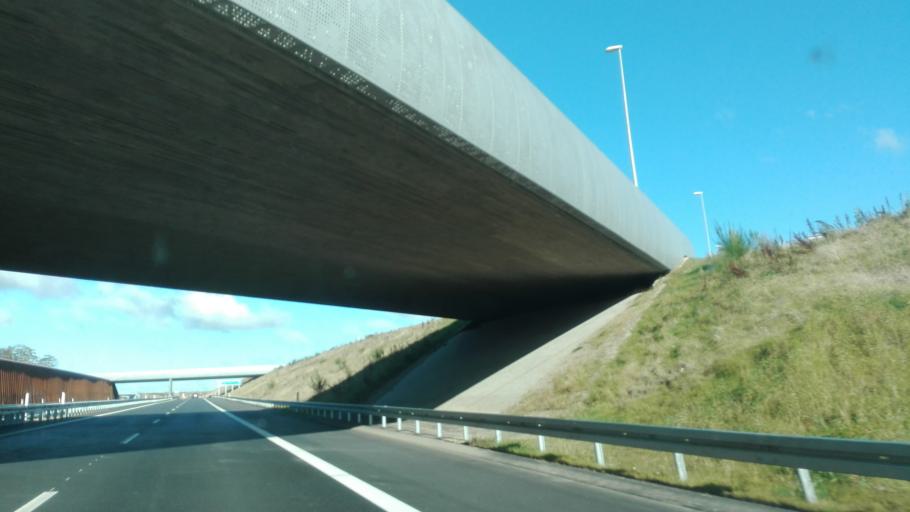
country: DK
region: Central Jutland
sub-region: Silkeborg Kommune
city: Silkeborg
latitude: 56.1961
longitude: 9.5592
